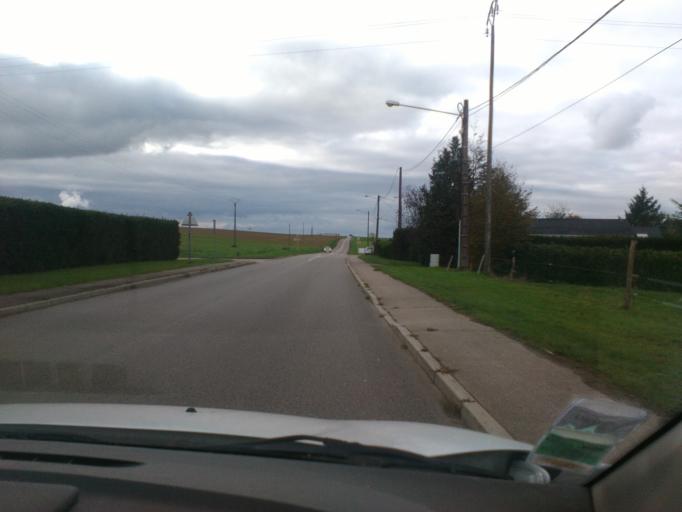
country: FR
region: Lorraine
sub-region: Departement des Vosges
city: Jeanmenil
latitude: 48.3475
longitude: 6.6771
